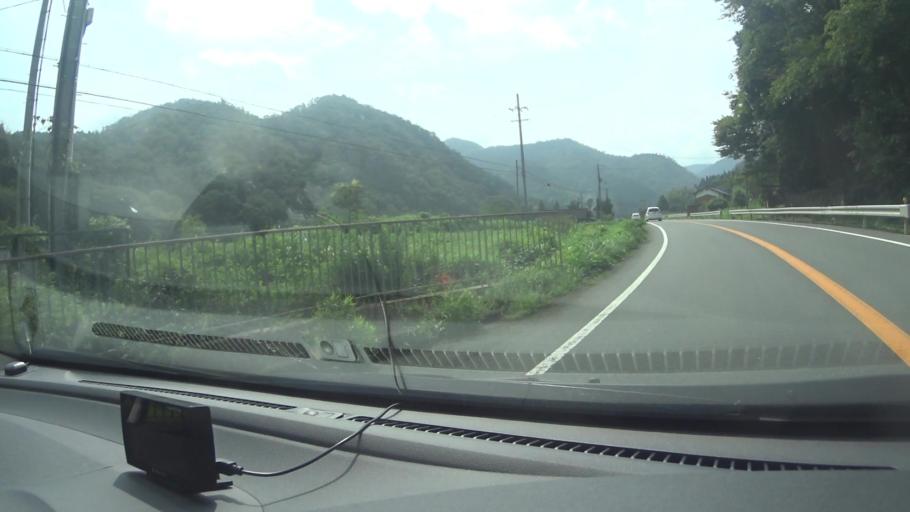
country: JP
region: Hyogo
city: Sasayama
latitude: 35.1590
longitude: 135.3531
